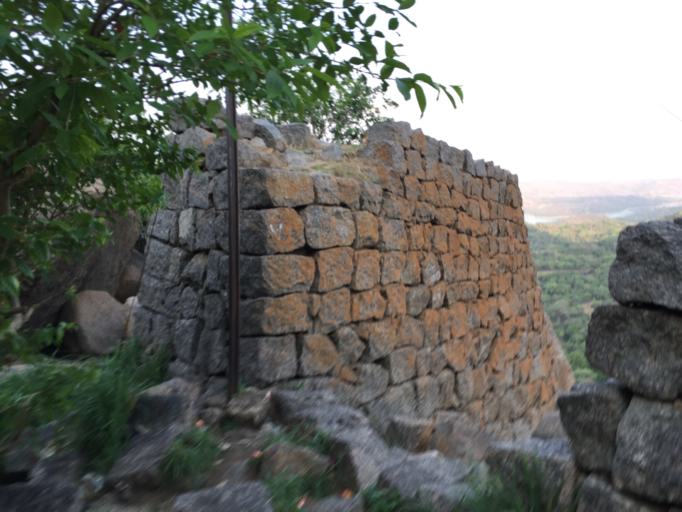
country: IN
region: Karnataka
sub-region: Ramanagara
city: Magadi
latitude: 12.9210
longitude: 77.2982
